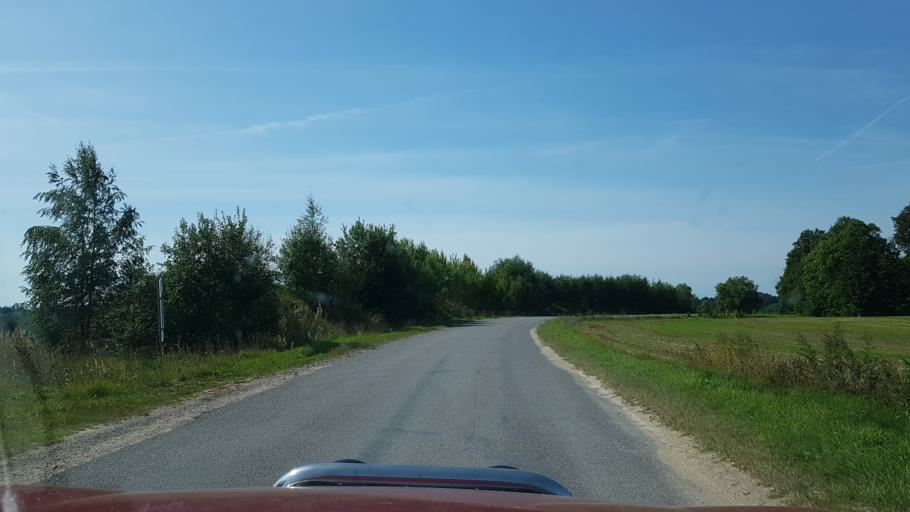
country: EE
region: Viljandimaa
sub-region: Vohma linn
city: Vohma
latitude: 58.5207
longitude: 25.6456
